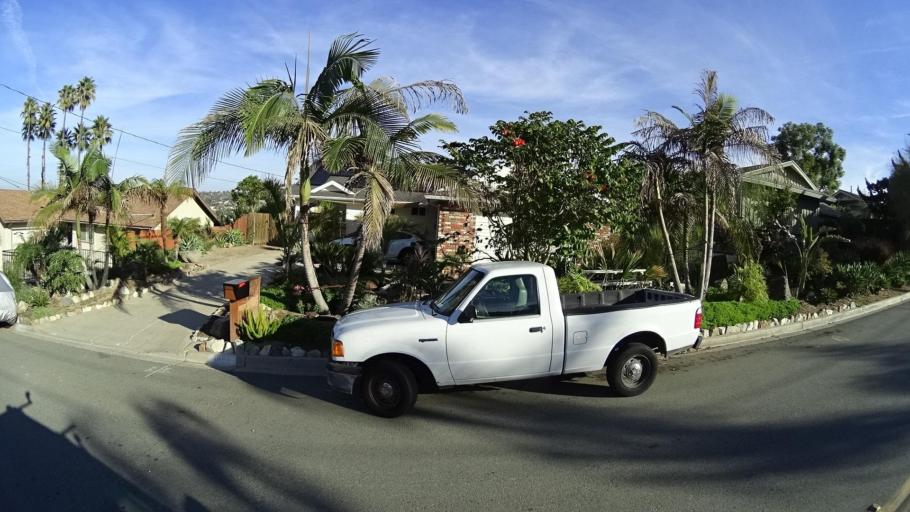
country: US
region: California
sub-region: San Diego County
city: Spring Valley
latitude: 32.7419
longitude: -116.9768
